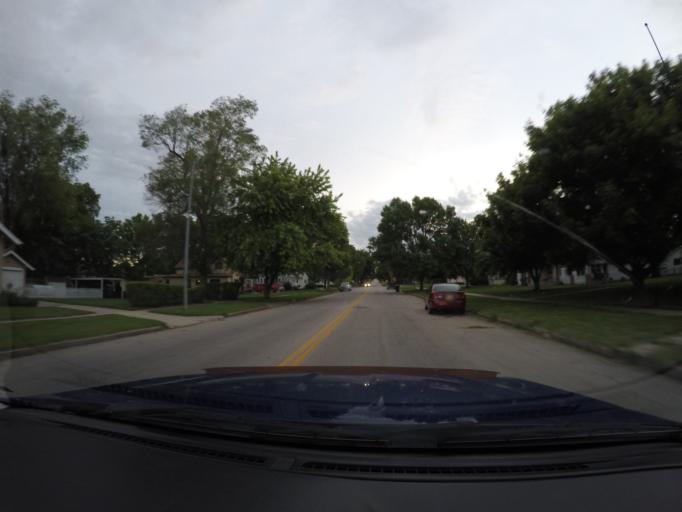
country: US
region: Nebraska
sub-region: Buffalo County
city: Kearney
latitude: 40.7046
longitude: -99.0872
